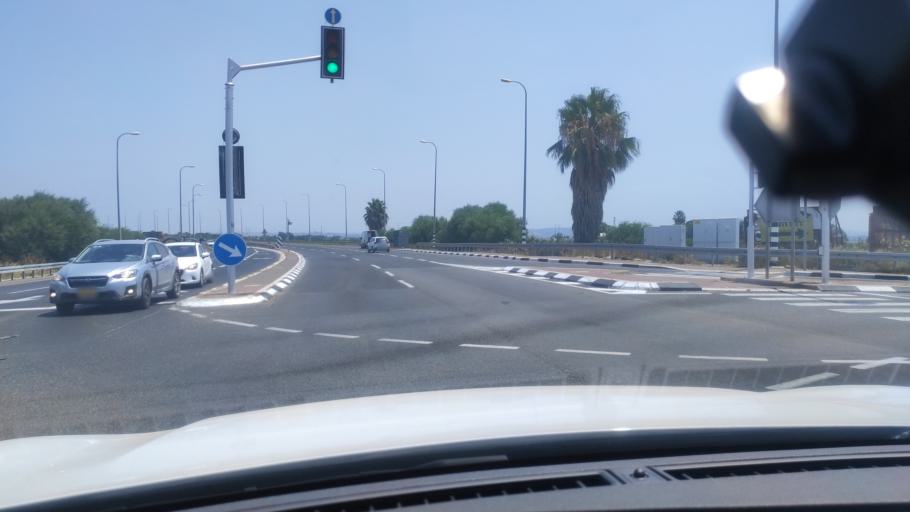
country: IL
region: Central District
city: Hod HaSharon
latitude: 32.1377
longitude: 34.9149
